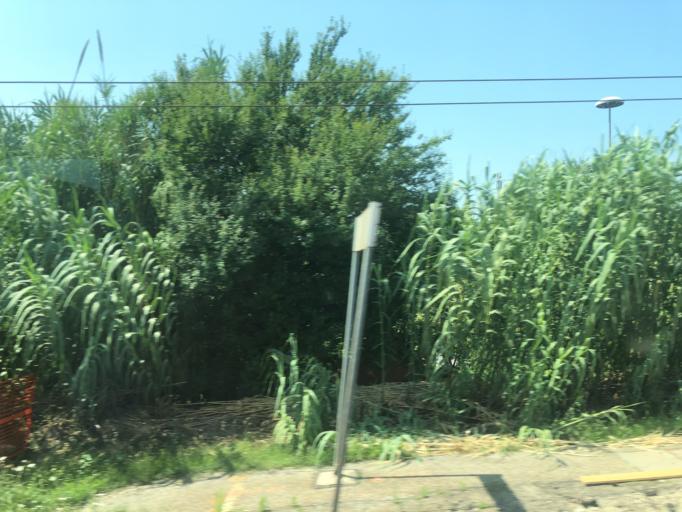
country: IT
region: Emilia-Romagna
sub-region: Forli-Cesena
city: Forli
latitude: 44.2230
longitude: 12.0577
